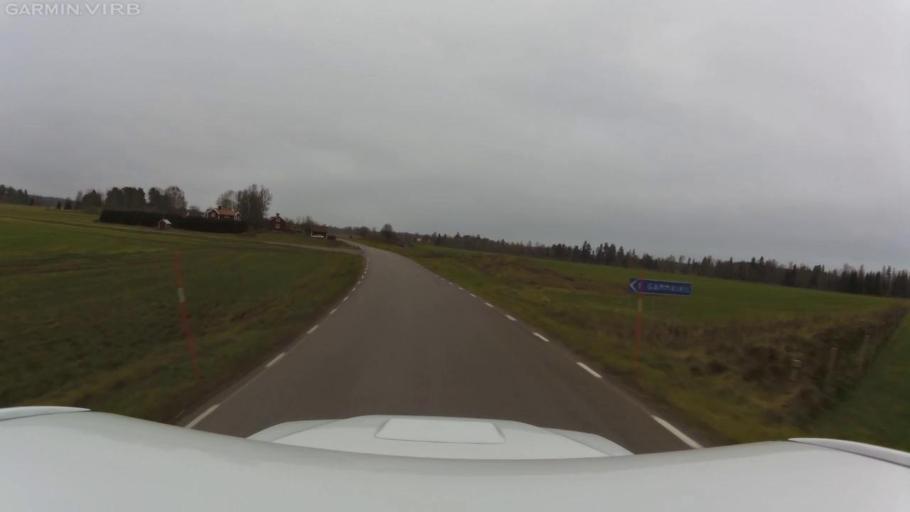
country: SE
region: OEstergoetland
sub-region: Linkopings Kommun
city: Vikingstad
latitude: 58.3058
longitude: 15.3811
